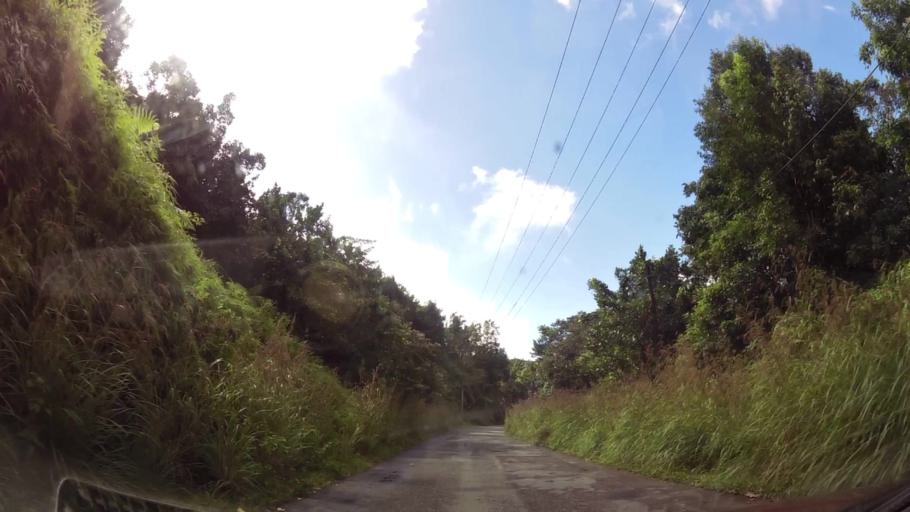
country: DM
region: Saint Paul
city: Pont Casse
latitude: 15.3885
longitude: -61.3337
